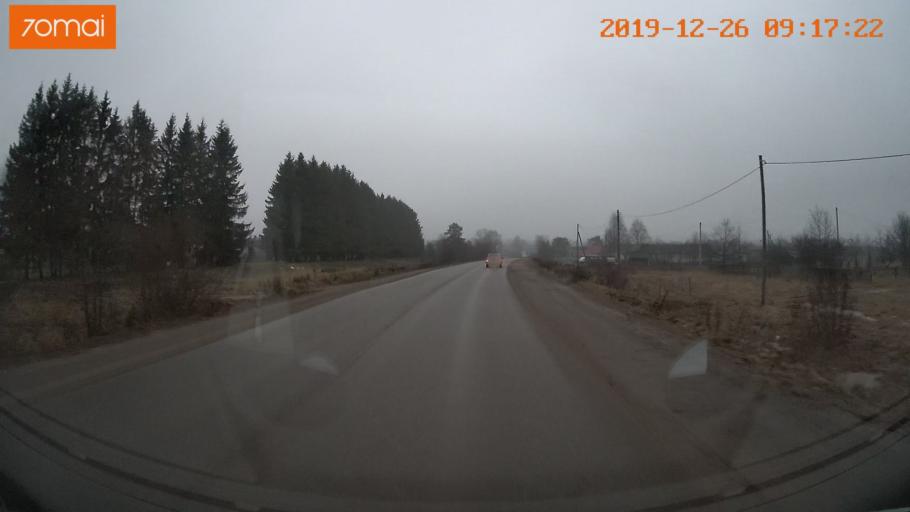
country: RU
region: Vologda
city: Gryazovets
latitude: 58.9289
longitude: 40.2388
